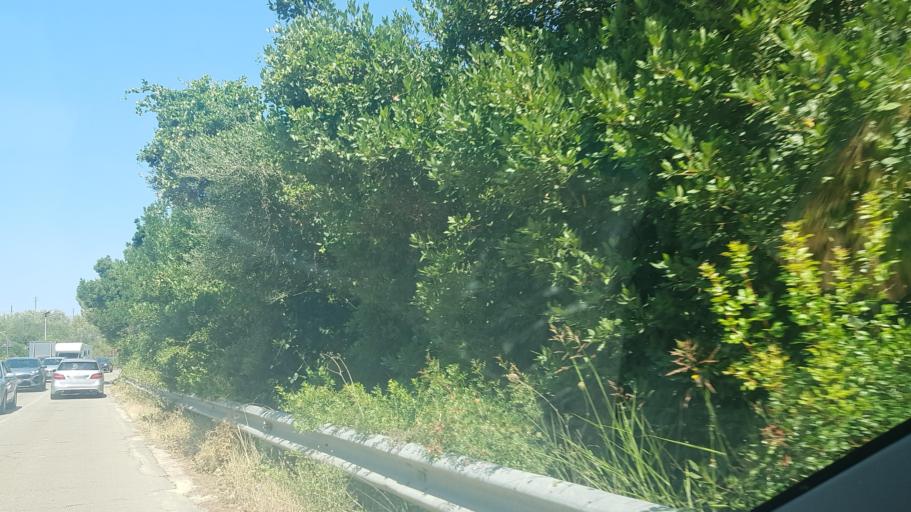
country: IT
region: Apulia
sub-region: Provincia di Lecce
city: Otranto
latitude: 40.1905
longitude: 18.4462
